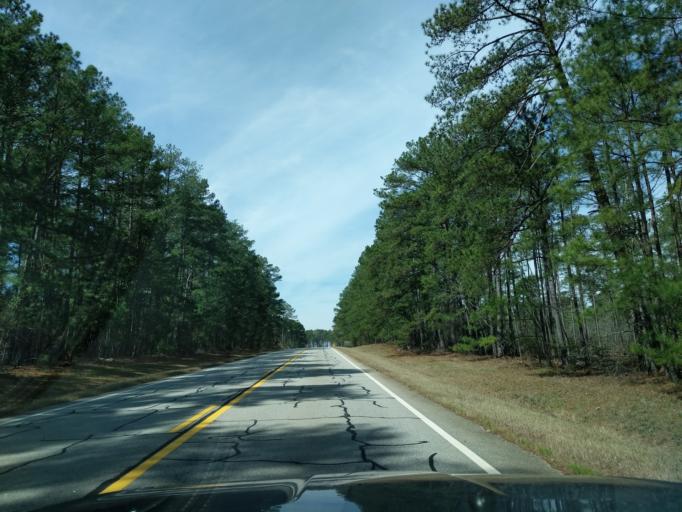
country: US
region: Georgia
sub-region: Columbia County
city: Appling
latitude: 33.6529
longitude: -82.2330
